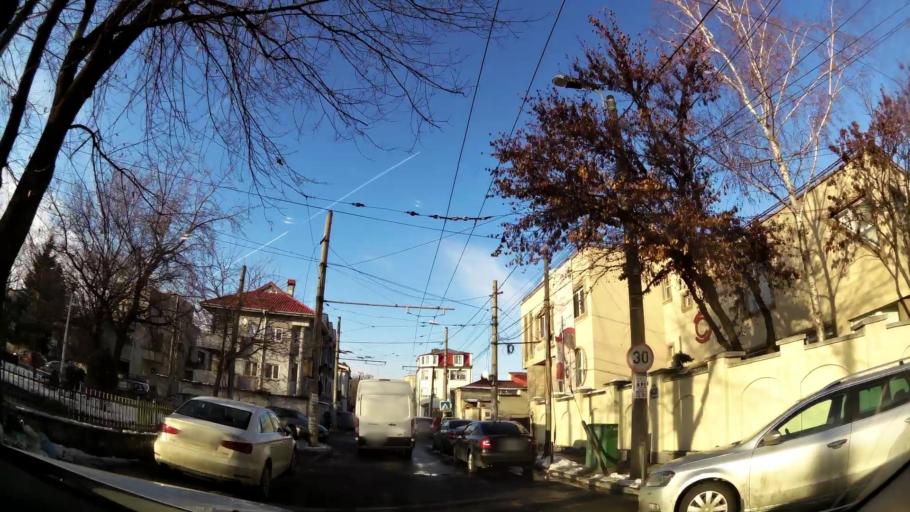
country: RO
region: Bucuresti
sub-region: Municipiul Bucuresti
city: Bucharest
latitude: 44.4354
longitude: 26.1261
